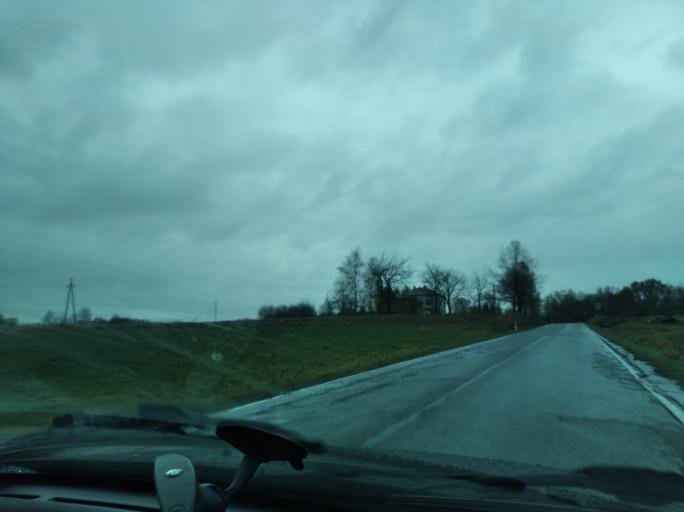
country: PL
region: Subcarpathian Voivodeship
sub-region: Powiat lancucki
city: Handzlowka
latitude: 49.9834
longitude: 22.1923
